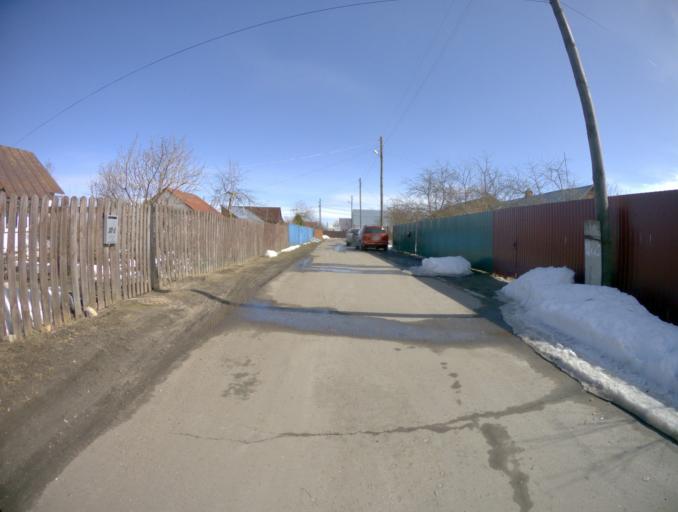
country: RU
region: Vladimir
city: Suzdal'
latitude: 56.4246
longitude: 40.4305
